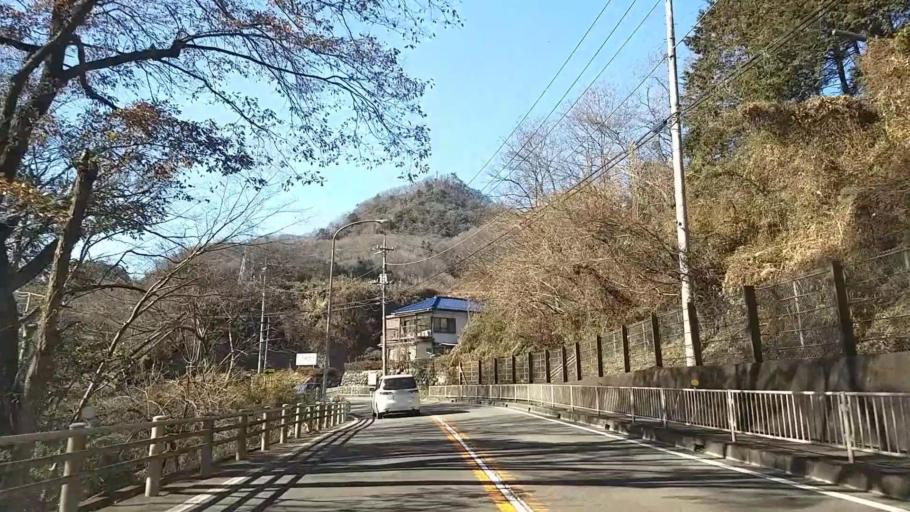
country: JP
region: Yamanashi
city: Uenohara
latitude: 35.6173
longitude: 139.0926
